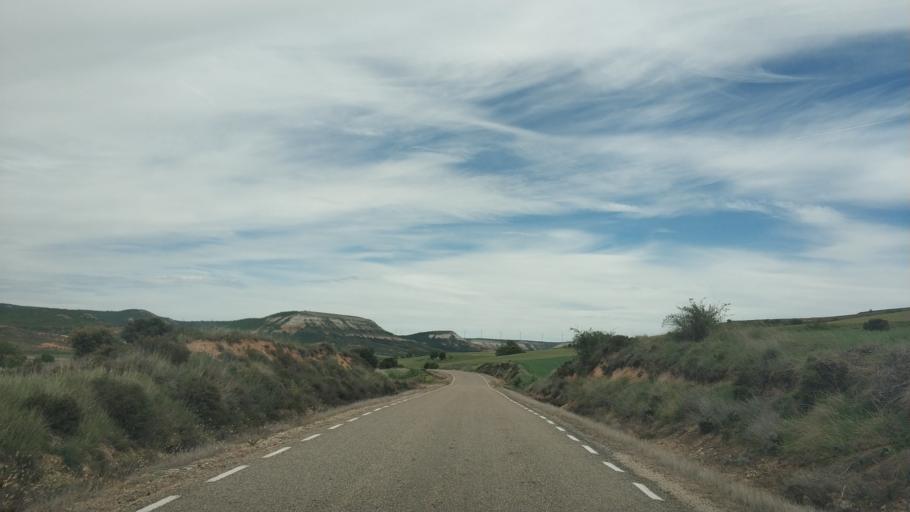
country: ES
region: Castille and Leon
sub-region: Provincia de Soria
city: Caltojar
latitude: 41.4332
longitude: -2.8041
